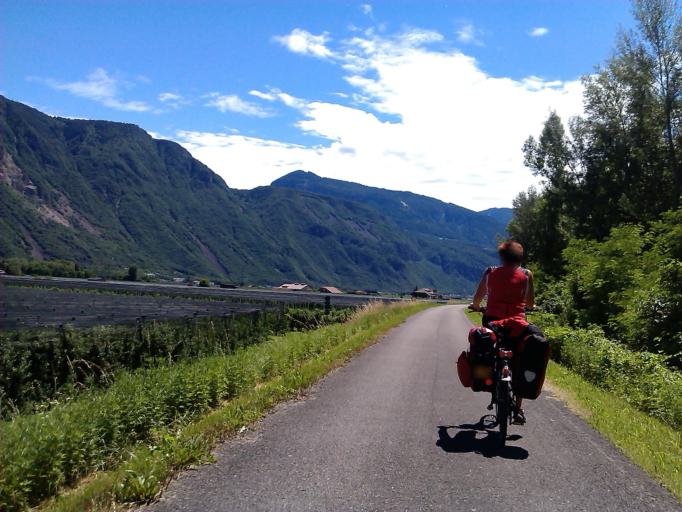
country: IT
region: Trentino-Alto Adige
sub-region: Bolzano
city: Vadena
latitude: 46.3920
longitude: 11.2976
